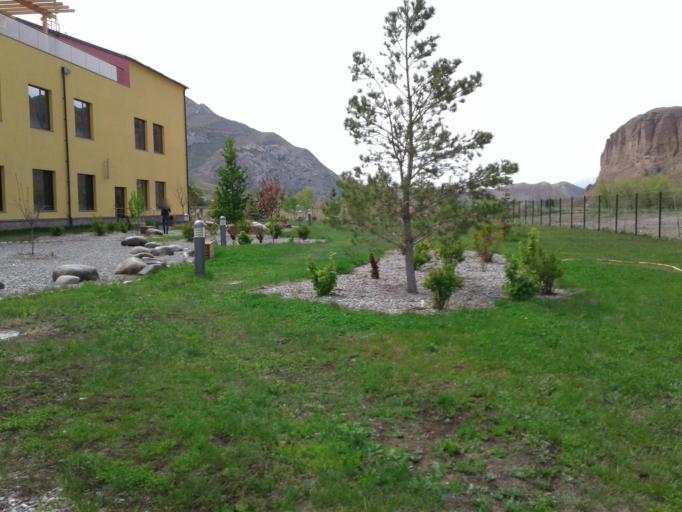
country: KG
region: Naryn
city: Naryn
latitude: 41.4300
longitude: 75.9011
